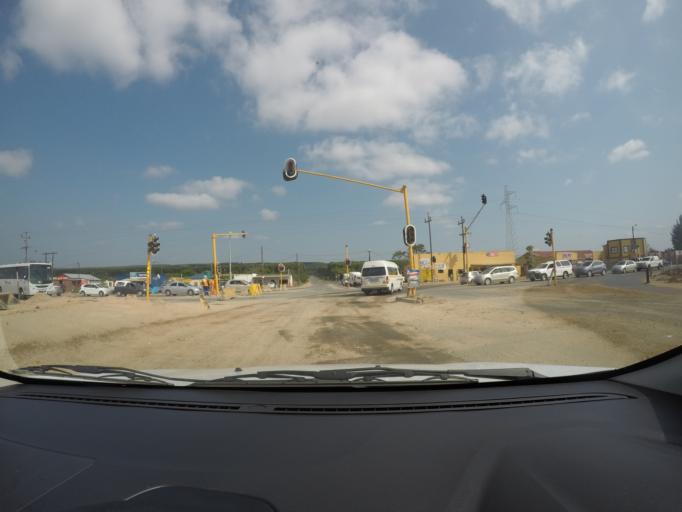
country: ZA
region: KwaZulu-Natal
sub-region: uThungulu District Municipality
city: eSikhawini
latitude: -28.8714
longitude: 31.9006
